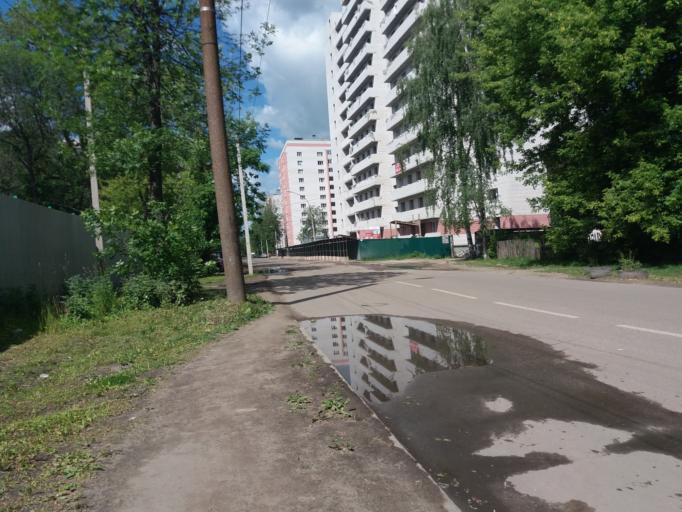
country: RU
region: Jaroslavl
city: Yaroslavl
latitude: 57.6404
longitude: 39.8467
